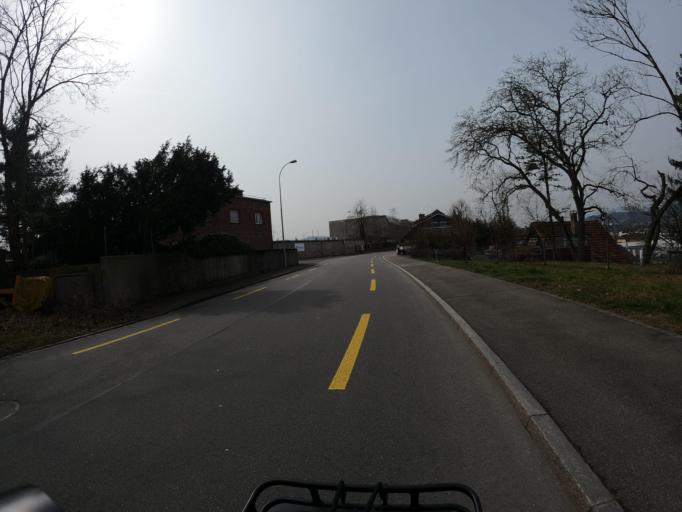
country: CH
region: Aargau
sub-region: Bezirk Aarau
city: Buchs
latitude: 47.3961
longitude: 8.0669
